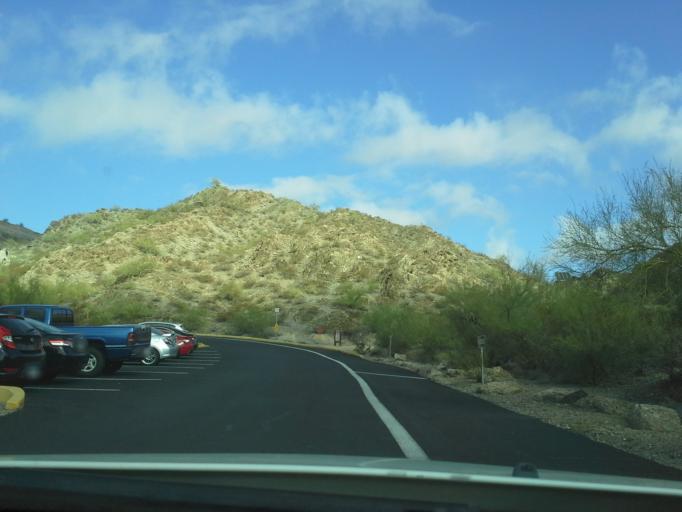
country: US
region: Arizona
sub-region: Maricopa County
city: Glendale
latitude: 33.5847
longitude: -112.0654
